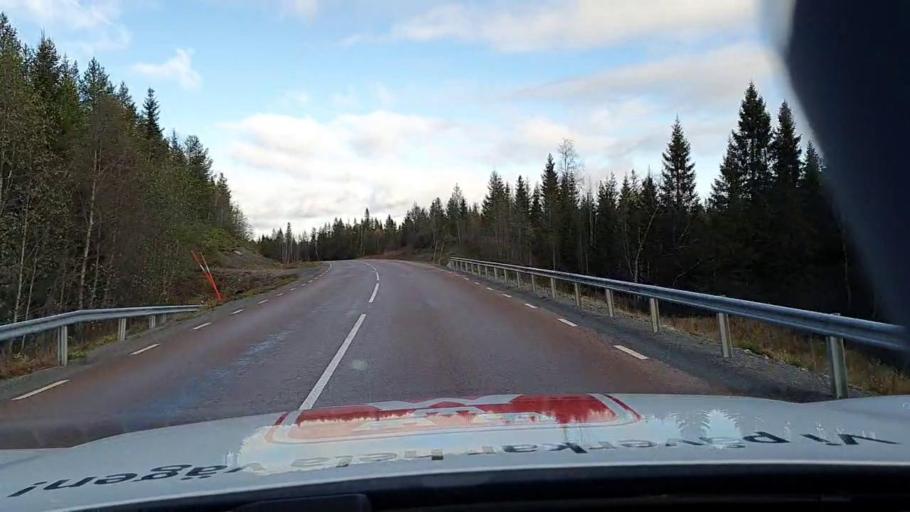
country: SE
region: Jaemtland
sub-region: Krokoms Kommun
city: Valla
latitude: 63.1558
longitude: 13.9711
